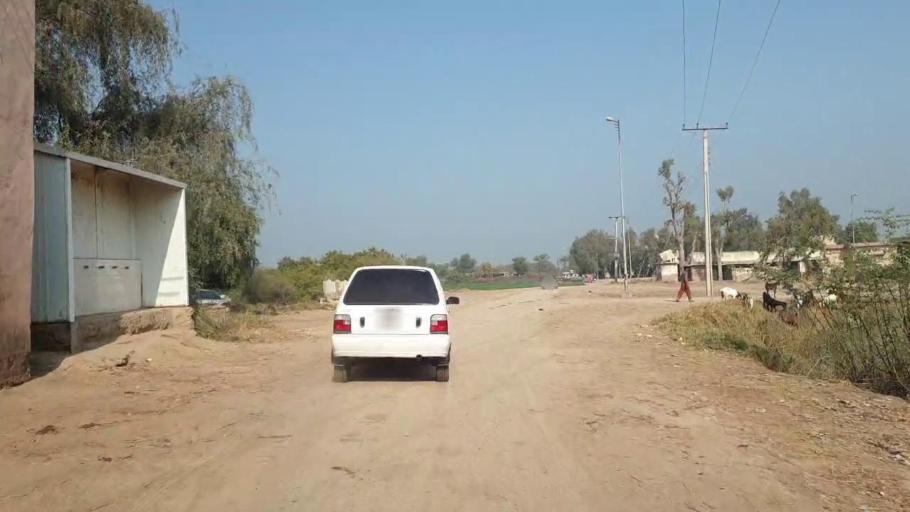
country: PK
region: Sindh
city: Bhit Shah
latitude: 25.7222
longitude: 68.5249
